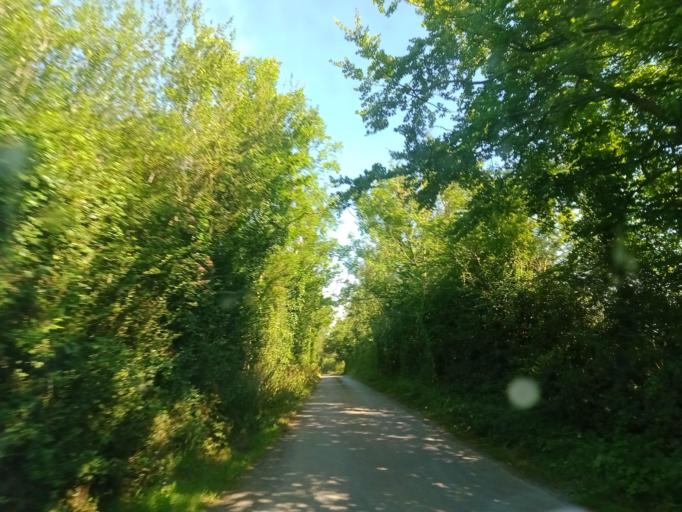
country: IE
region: Leinster
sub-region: Kilkenny
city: Ballyragget
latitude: 52.7883
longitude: -7.4226
